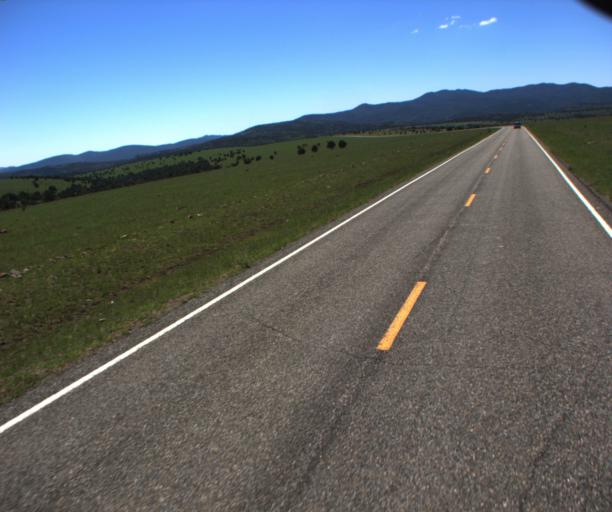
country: US
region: Arizona
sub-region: Greenlee County
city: Morenci
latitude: 33.3265
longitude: -109.3509
